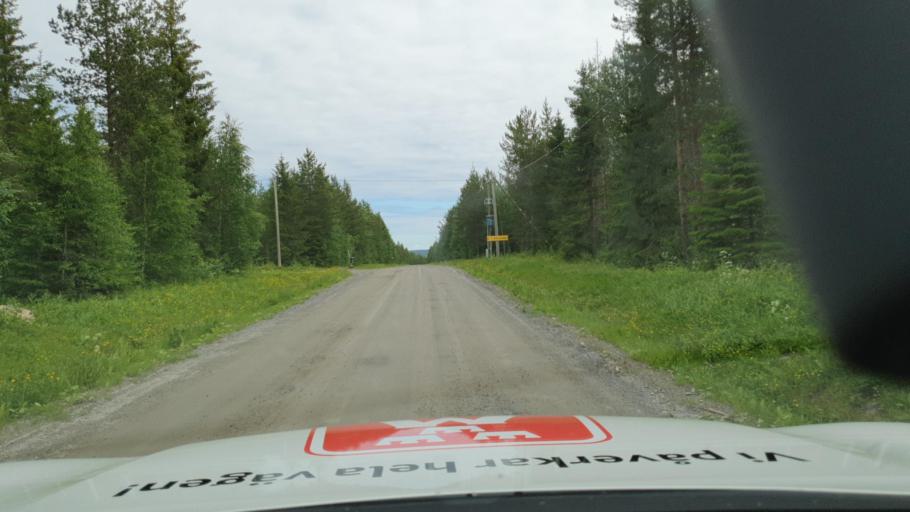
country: SE
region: Vaesterbotten
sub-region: Skelleftea Kommun
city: Langsele
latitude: 64.5013
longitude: 20.2732
